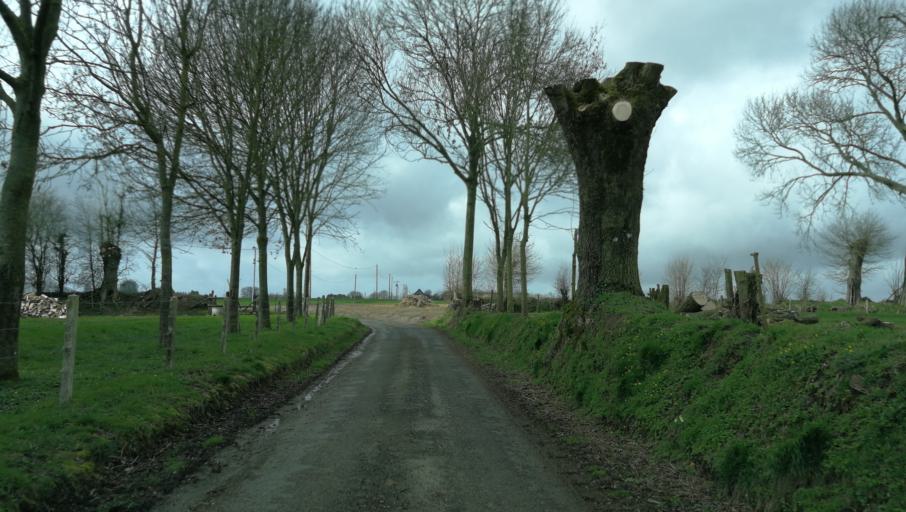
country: FR
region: Haute-Normandie
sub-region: Departement de l'Eure
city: Lieurey
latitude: 49.2326
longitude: 0.5365
